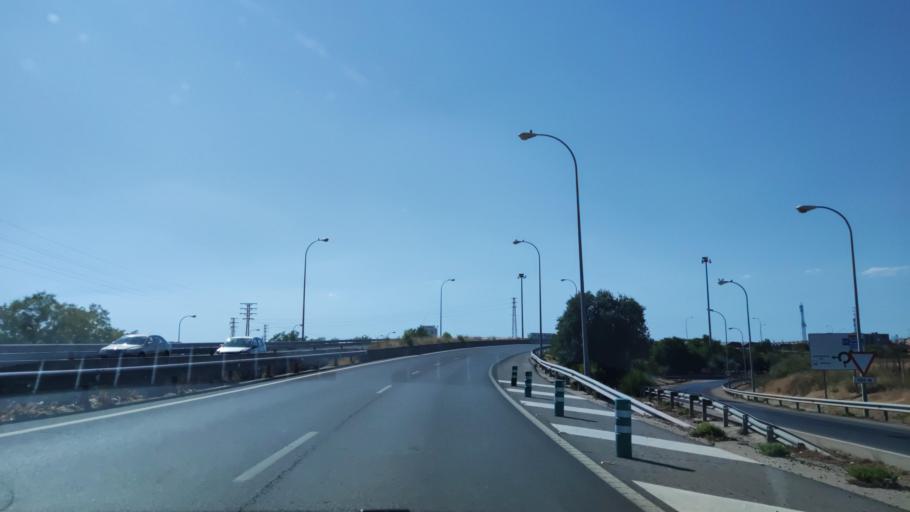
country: ES
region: Madrid
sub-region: Provincia de Madrid
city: Alcorcon
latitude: 40.3404
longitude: -3.7978
